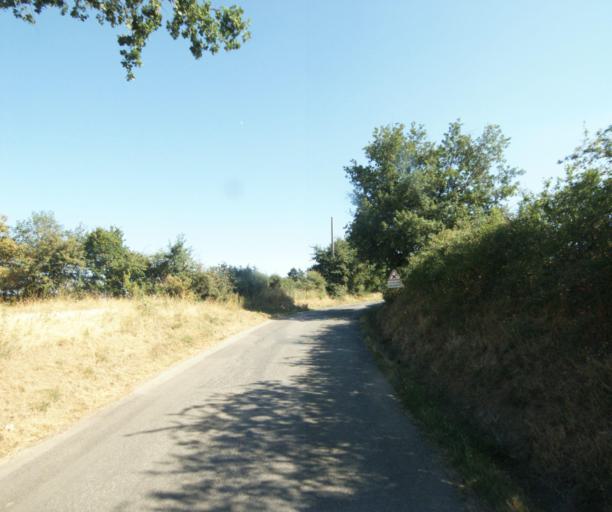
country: FR
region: Rhone-Alpes
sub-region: Departement du Rhone
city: Lentilly
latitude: 45.8127
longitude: 4.6777
